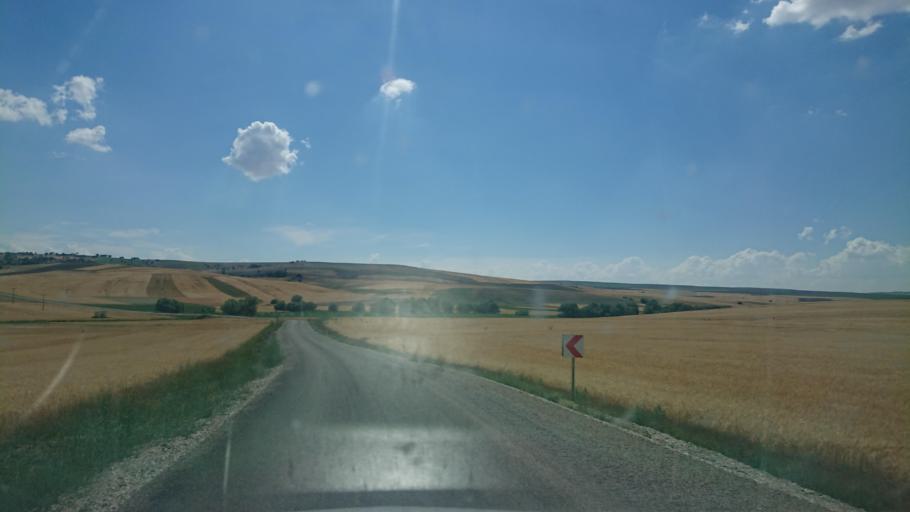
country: TR
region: Aksaray
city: Agacoren
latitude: 38.7848
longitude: 33.7985
